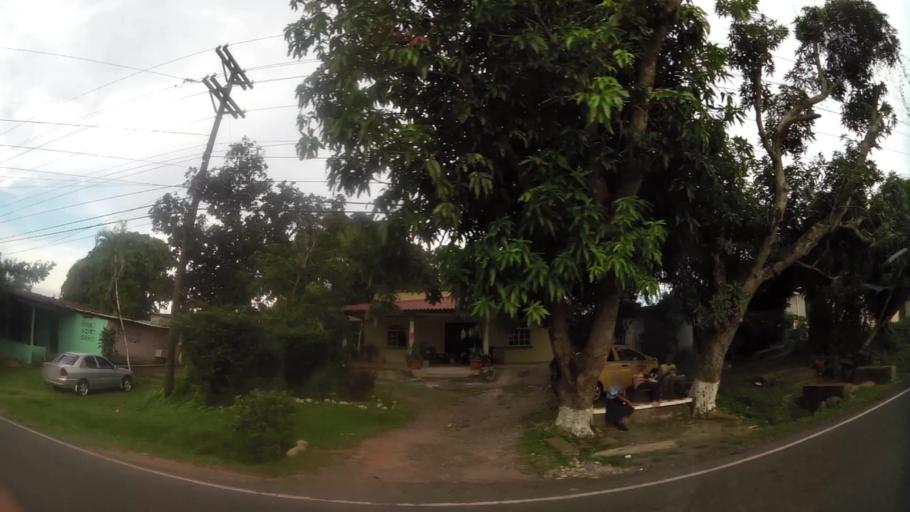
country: PA
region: Panama
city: La Chorrera
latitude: 8.8932
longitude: -79.7787
